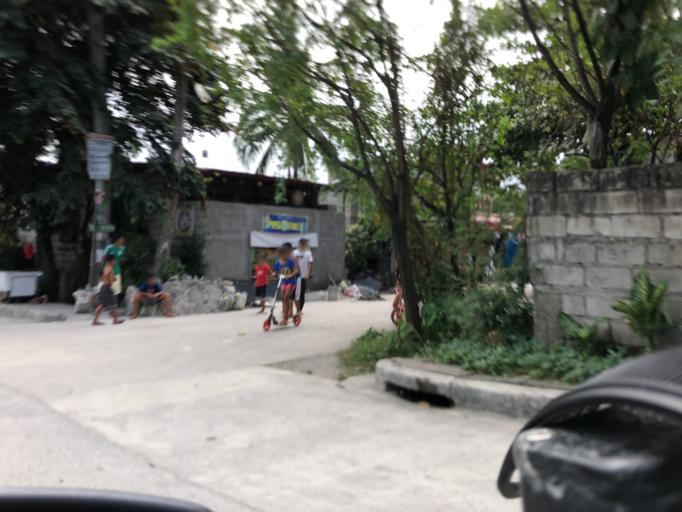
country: PH
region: Central Luzon
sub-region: Province of Bulacan
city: San Jose del Monte
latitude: 14.7509
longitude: 121.0572
